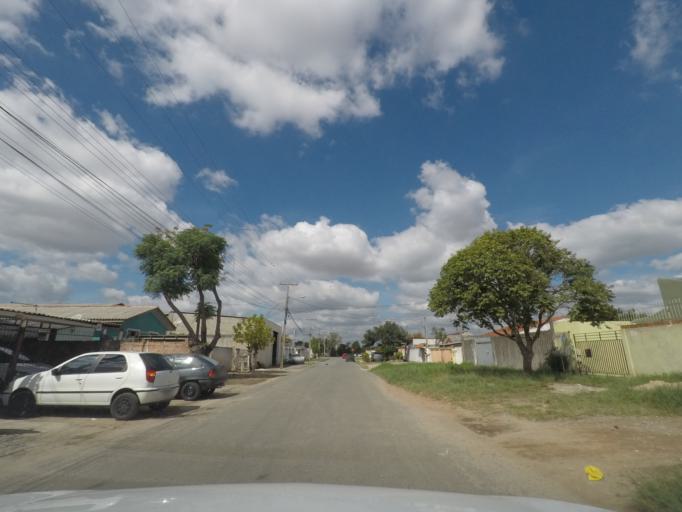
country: BR
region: Parana
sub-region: Sao Jose Dos Pinhais
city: Sao Jose dos Pinhais
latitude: -25.5069
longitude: -49.2164
